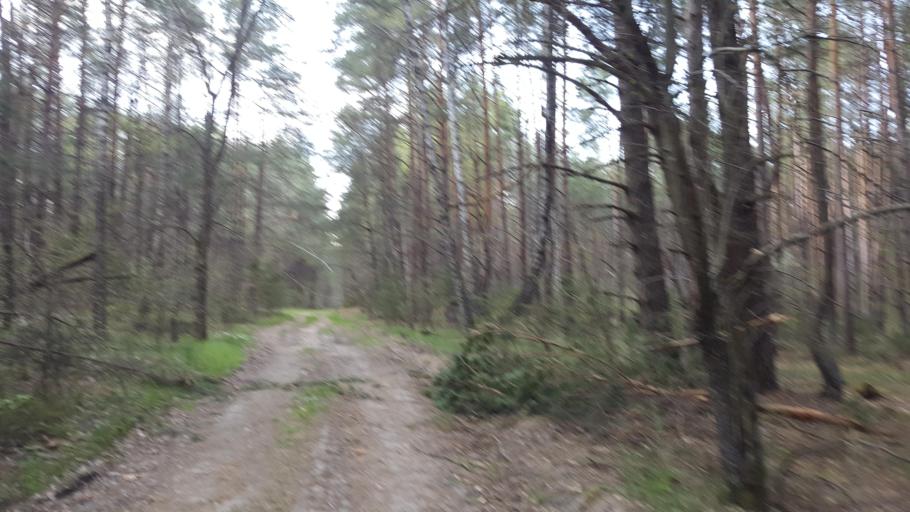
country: BY
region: Brest
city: Kamyanyets
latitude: 52.3528
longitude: 23.8394
